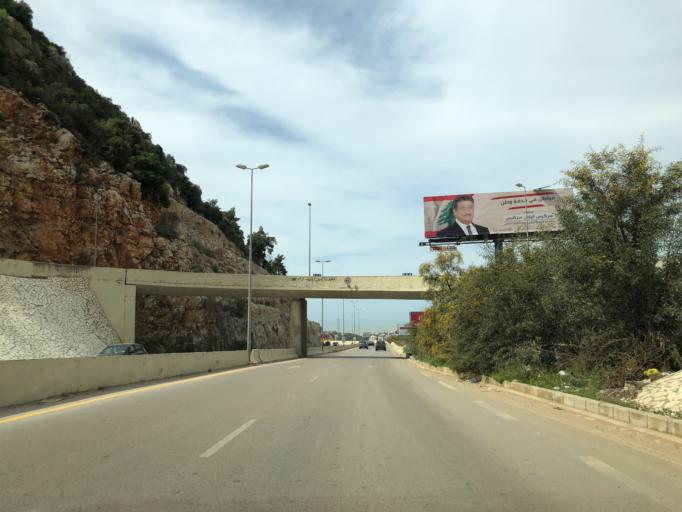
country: LB
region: Mont-Liban
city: Jdaidet el Matn
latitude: 33.8974
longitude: 35.6484
